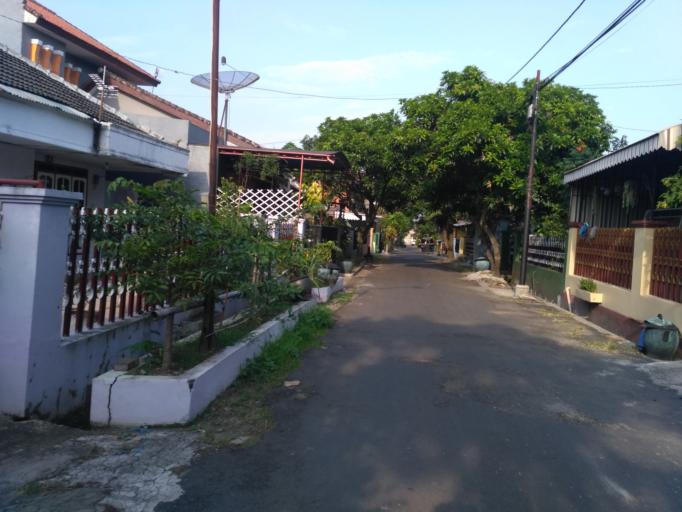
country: ID
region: East Java
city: Malang
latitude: -7.9398
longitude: 112.6276
